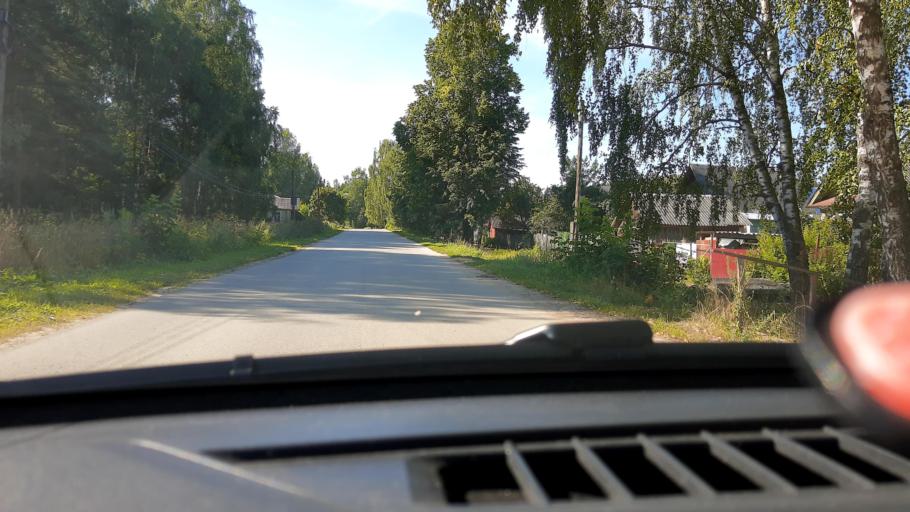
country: RU
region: Nizjnij Novgorod
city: Neklyudovo
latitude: 56.5376
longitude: 43.8311
